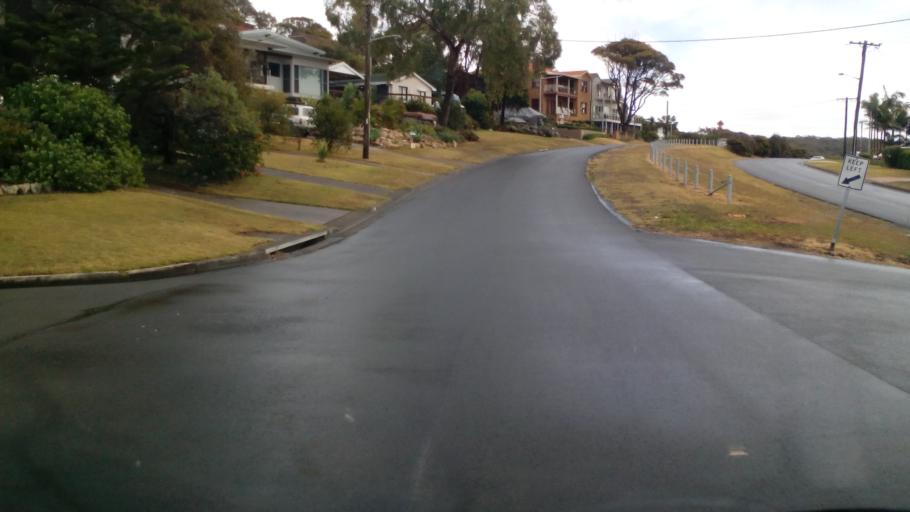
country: AU
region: New South Wales
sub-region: Lake Macquarie Shire
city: Belmont South
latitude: -33.1099
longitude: 151.6422
